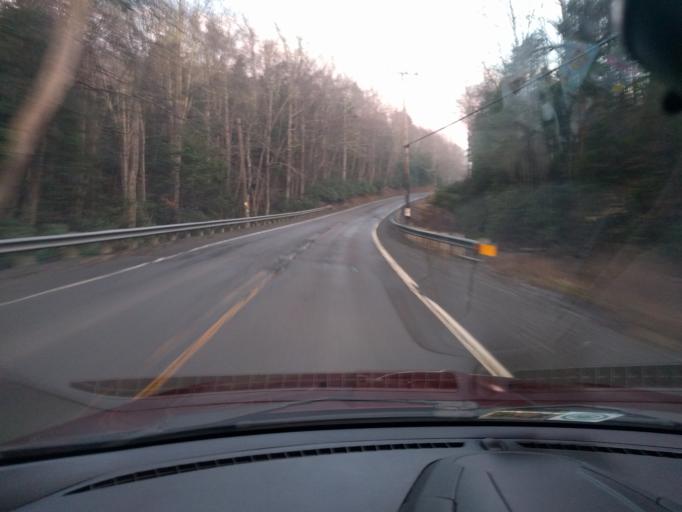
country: US
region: West Virginia
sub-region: Greenbrier County
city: Rainelle
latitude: 38.0392
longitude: -80.9218
